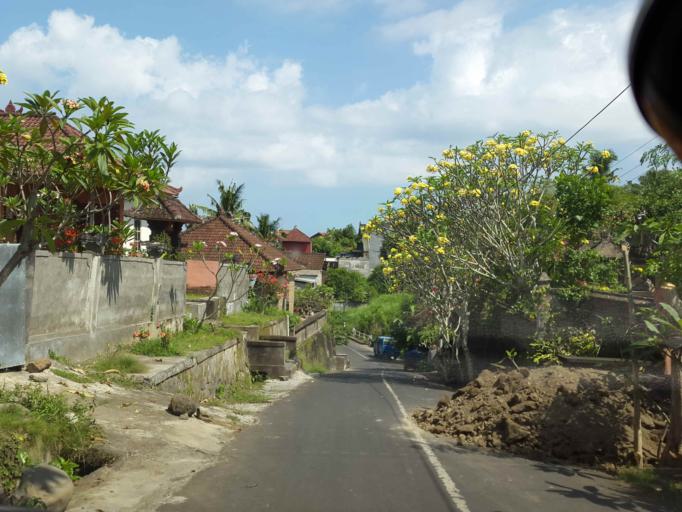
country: ID
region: Bali
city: Klungkung
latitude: -8.5467
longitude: 115.3782
